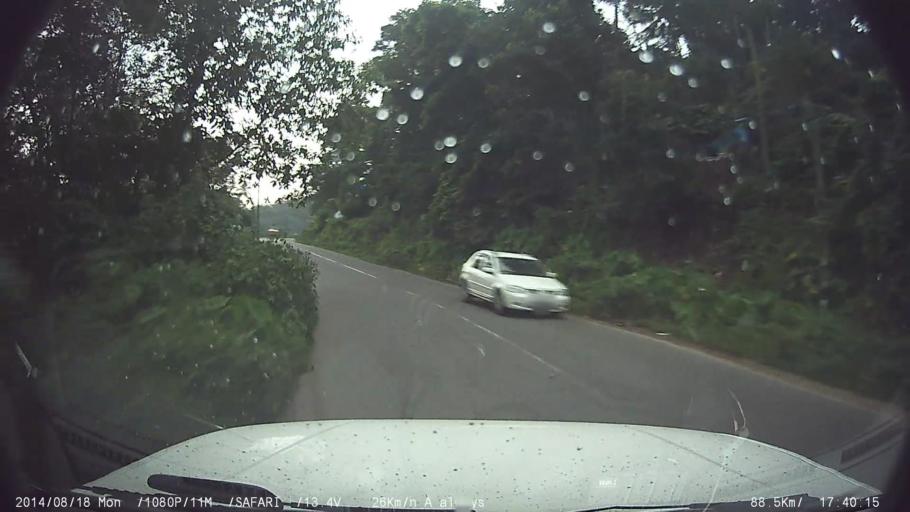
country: IN
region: Kerala
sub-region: Ernakulam
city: Muvattupuzha
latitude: 9.9238
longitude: 76.5830
